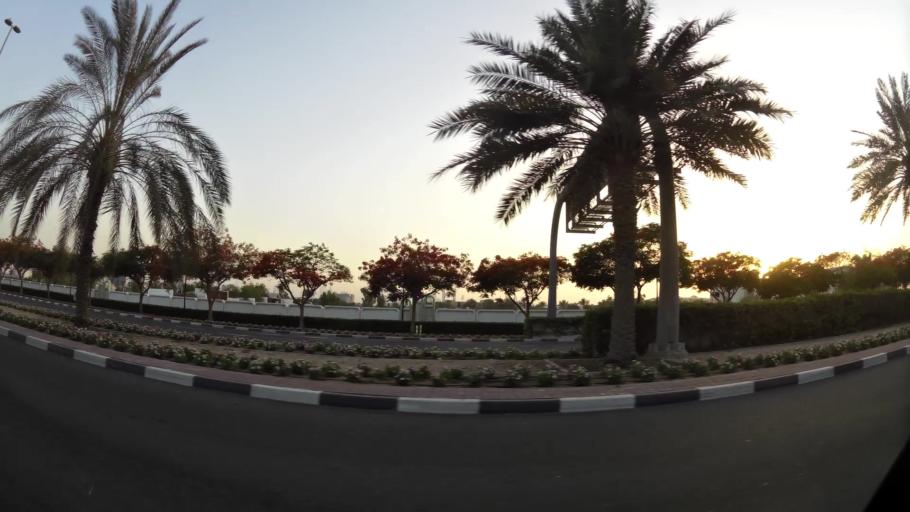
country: AE
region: Ash Shariqah
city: Sharjah
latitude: 25.2425
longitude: 55.3231
